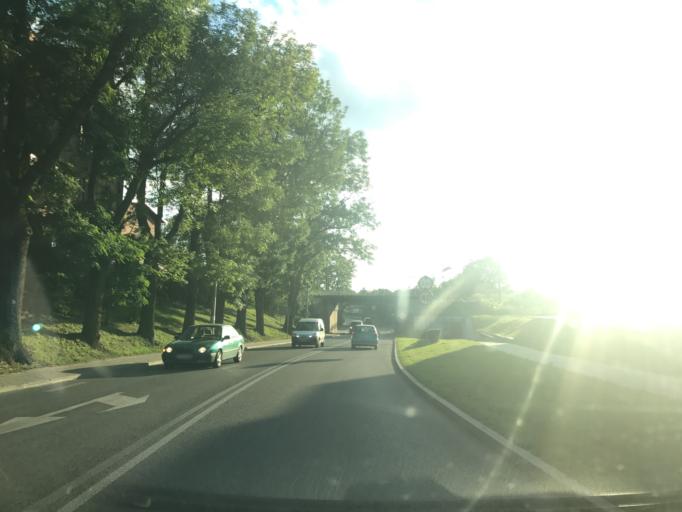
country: PL
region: Greater Poland Voivodeship
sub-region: Powiat jarocinski
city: Jarocin
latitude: 51.9726
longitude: 17.4962
